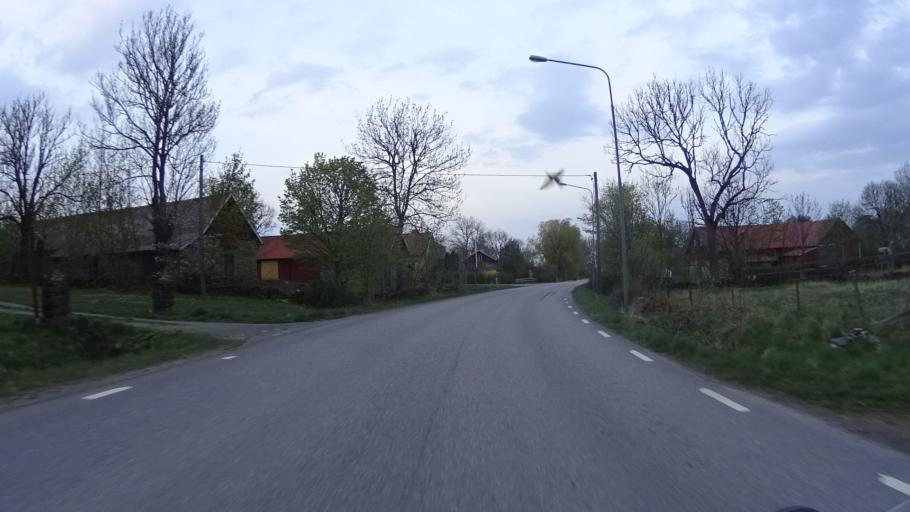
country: SE
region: Vaestra Goetaland
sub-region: Gotene Kommun
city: Kallby
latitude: 58.5588
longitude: 13.3501
